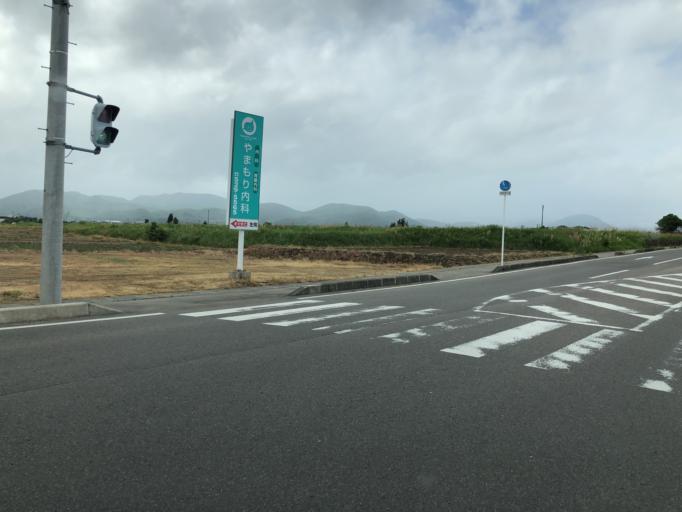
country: JP
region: Fukushima
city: Fukushima-shi
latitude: 37.7712
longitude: 140.4345
